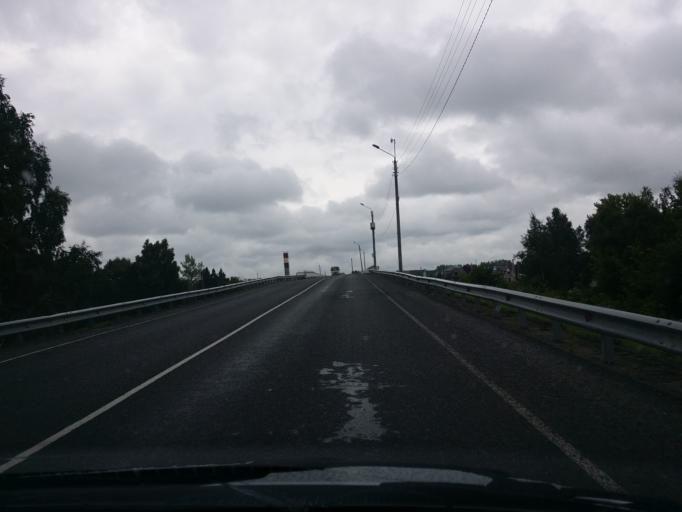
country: RU
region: Altai Krai
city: Vlasikha
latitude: 53.3547
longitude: 83.5524
